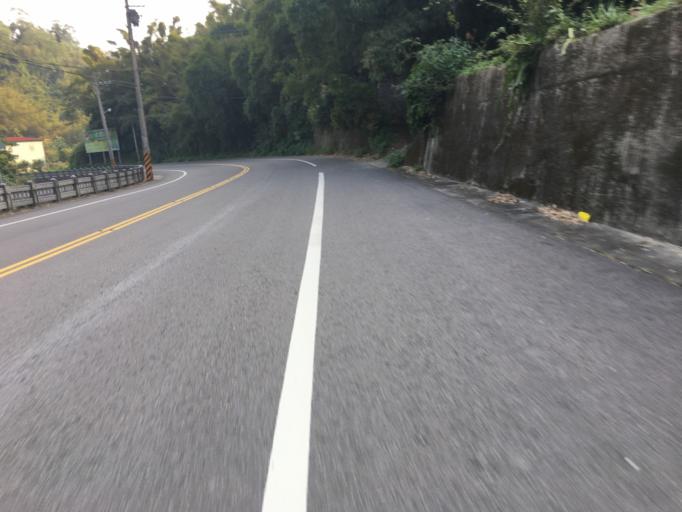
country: TW
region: Taiwan
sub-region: Hsinchu
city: Hsinchu
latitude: 24.7323
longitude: 121.0284
